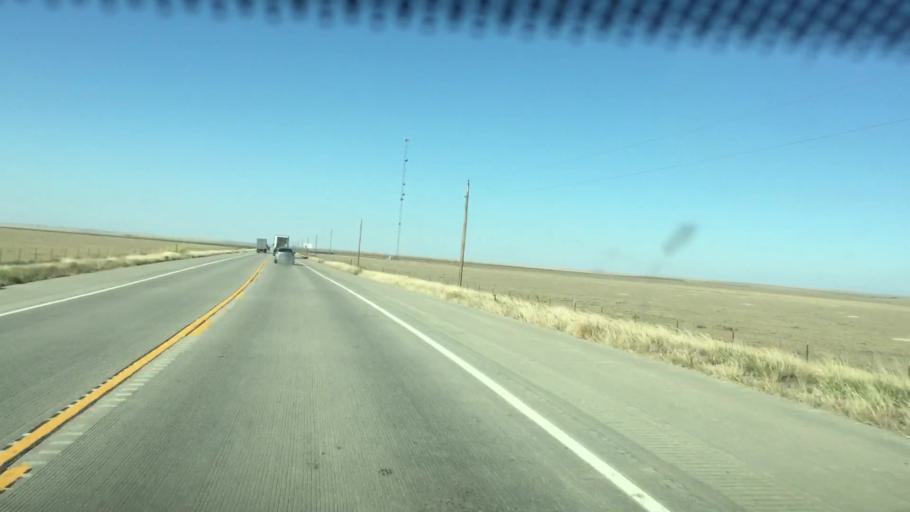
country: US
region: Colorado
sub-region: Prowers County
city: Lamar
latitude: 38.2758
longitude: -102.7198
